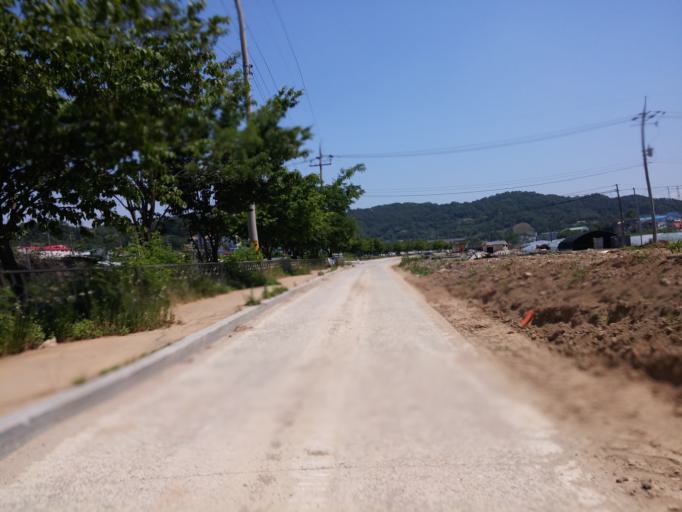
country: KR
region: Chungcheongbuk-do
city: Cheongju-si
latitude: 36.5577
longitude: 127.4338
